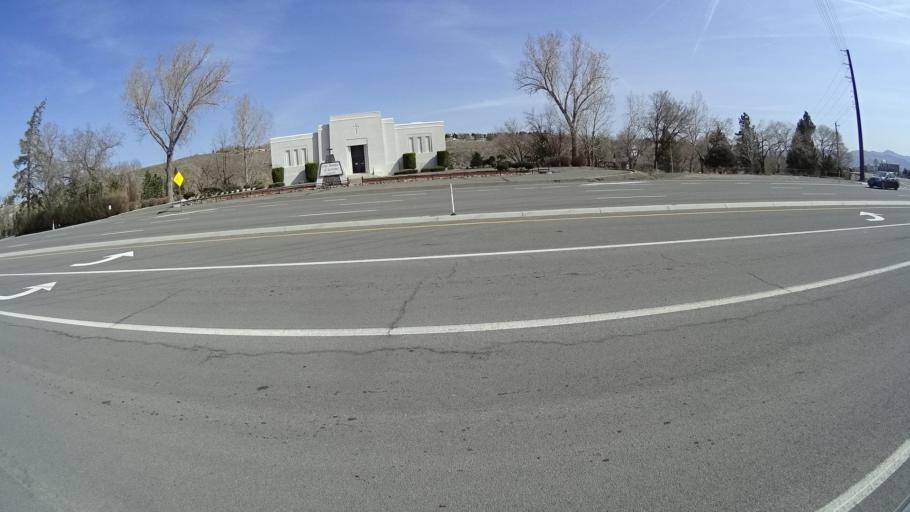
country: US
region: Nevada
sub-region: Washoe County
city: Reno
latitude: 39.5513
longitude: -119.8236
